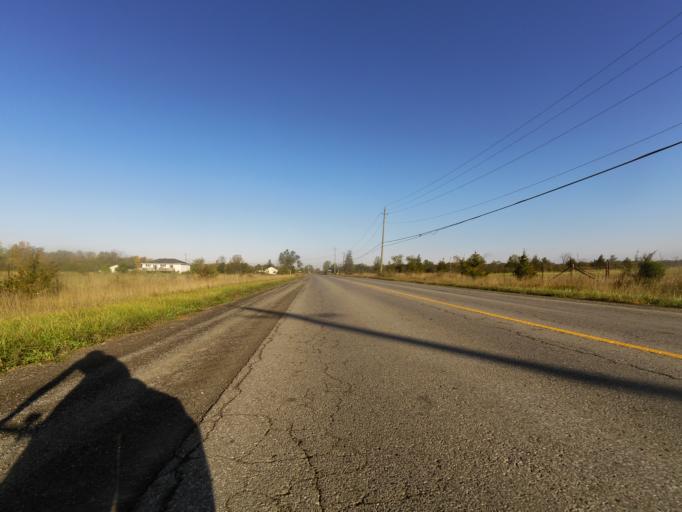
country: CA
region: Ontario
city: Belleville
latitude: 44.0446
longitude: -77.3821
